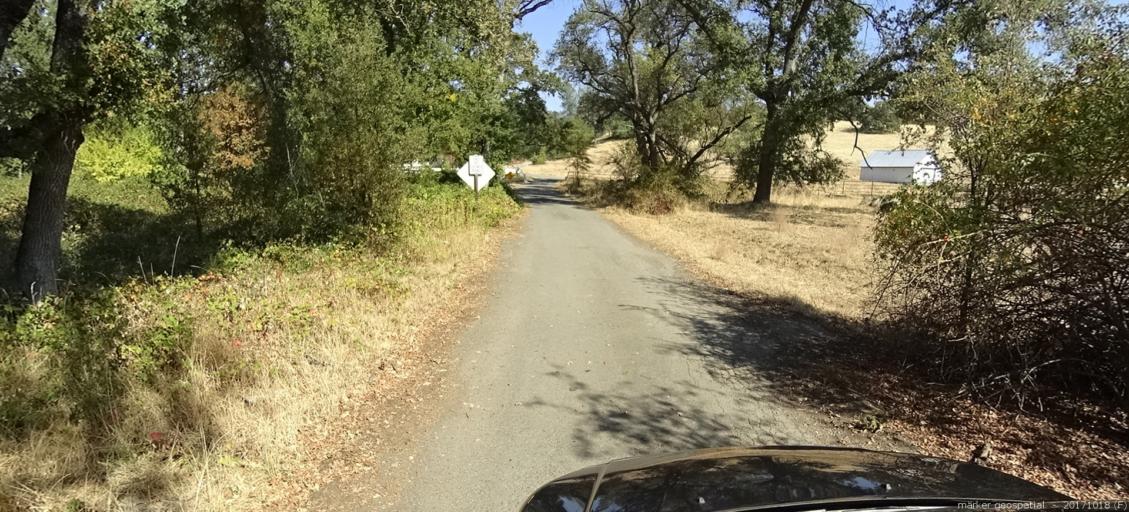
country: US
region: California
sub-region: Shasta County
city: Shingletown
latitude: 40.5653
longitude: -122.0280
